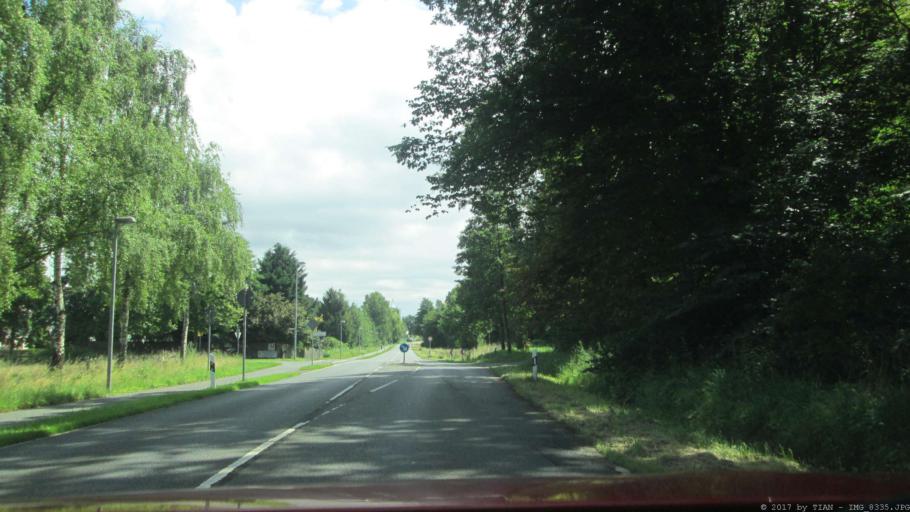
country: DE
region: Lower Saxony
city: Wolfsburg
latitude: 52.4214
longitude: 10.8345
